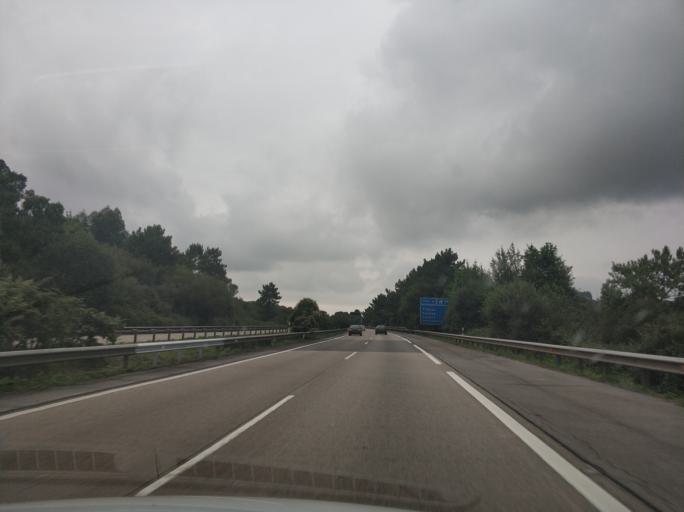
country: ES
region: Asturias
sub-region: Province of Asturias
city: Corvera de Asturias
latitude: 43.5238
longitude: -5.8239
